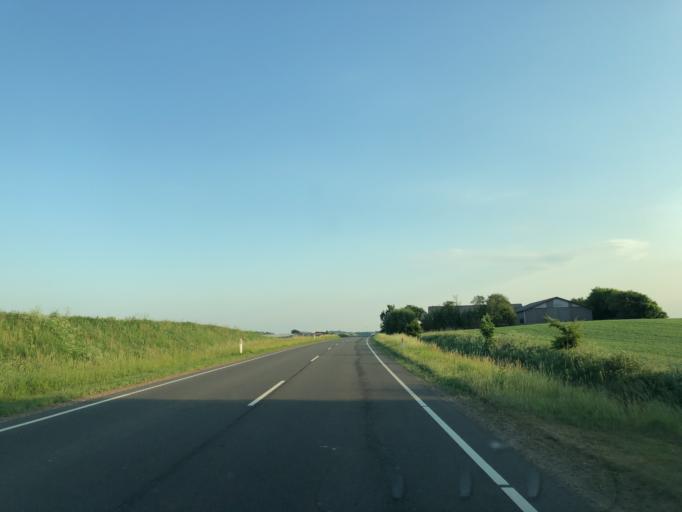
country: DK
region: Central Jutland
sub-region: Struer Kommune
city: Struer
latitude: 56.4628
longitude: 8.5454
